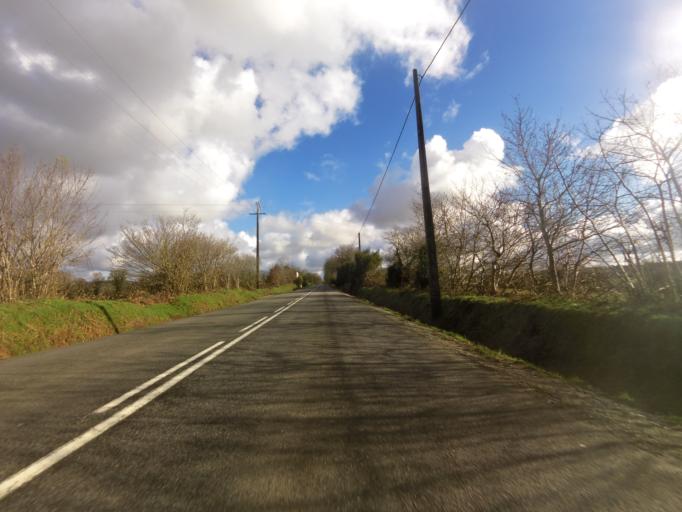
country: FR
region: Brittany
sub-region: Departement du Morbihan
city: Gourin
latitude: 48.1412
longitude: -3.5650
